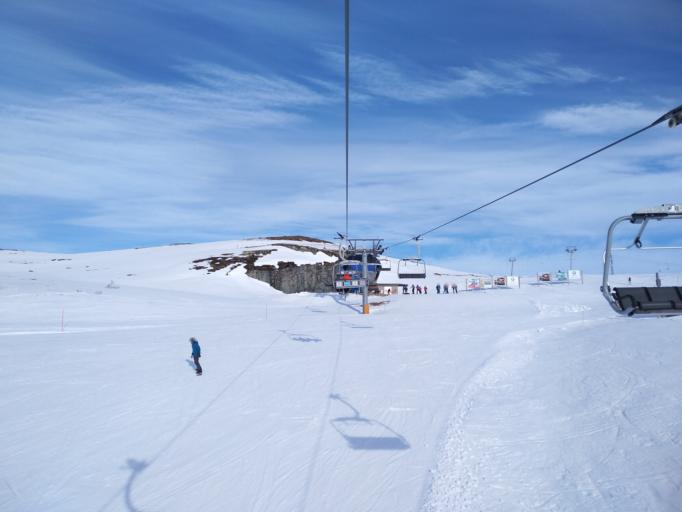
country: NO
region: Aust-Agder
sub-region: Bykle
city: Hovden
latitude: 59.5778
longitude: 7.3205
